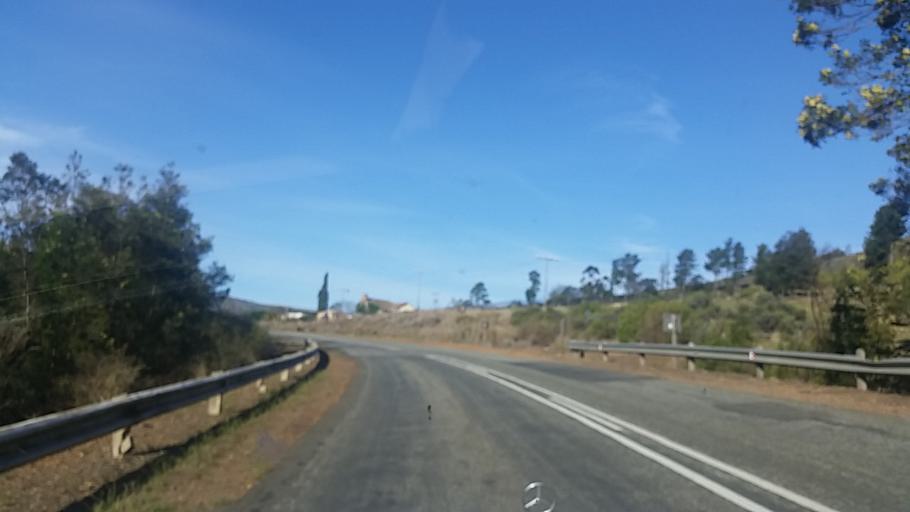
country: ZA
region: Western Cape
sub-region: Eden District Municipality
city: Knysna
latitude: -33.7742
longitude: 22.9577
